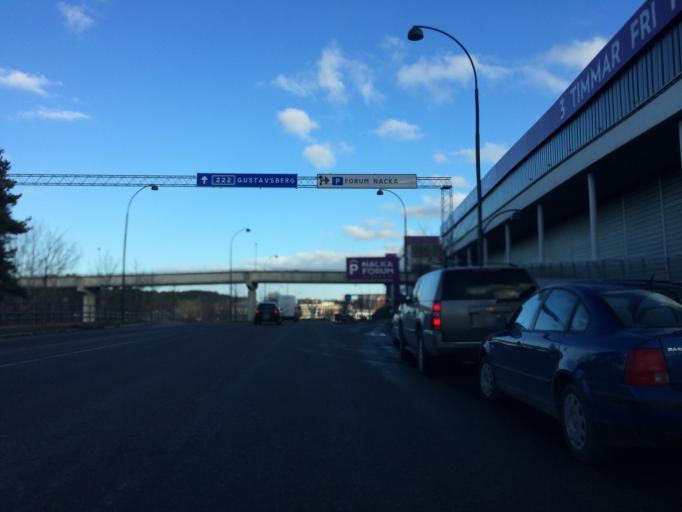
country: SE
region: Stockholm
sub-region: Nacka Kommun
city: Nacka
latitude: 59.3108
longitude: 18.1651
